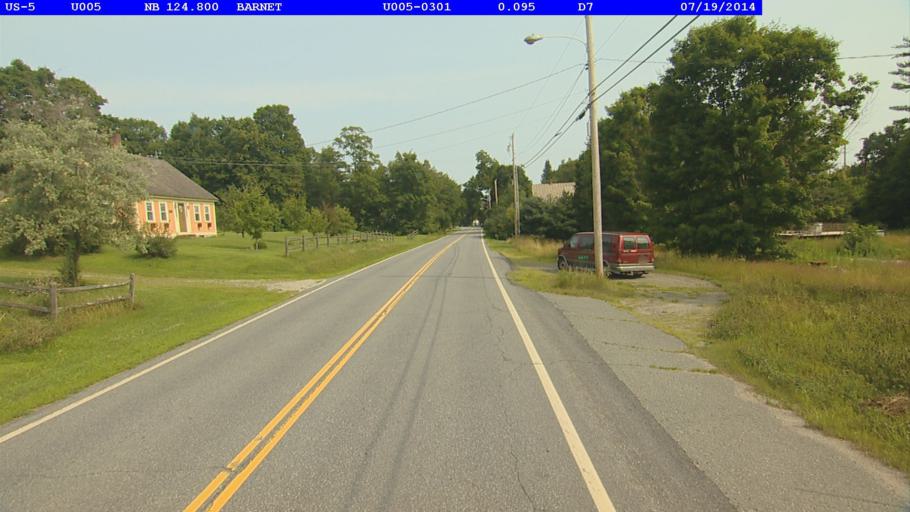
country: US
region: New Hampshire
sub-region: Grafton County
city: Woodsville
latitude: 44.2580
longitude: -72.0619
